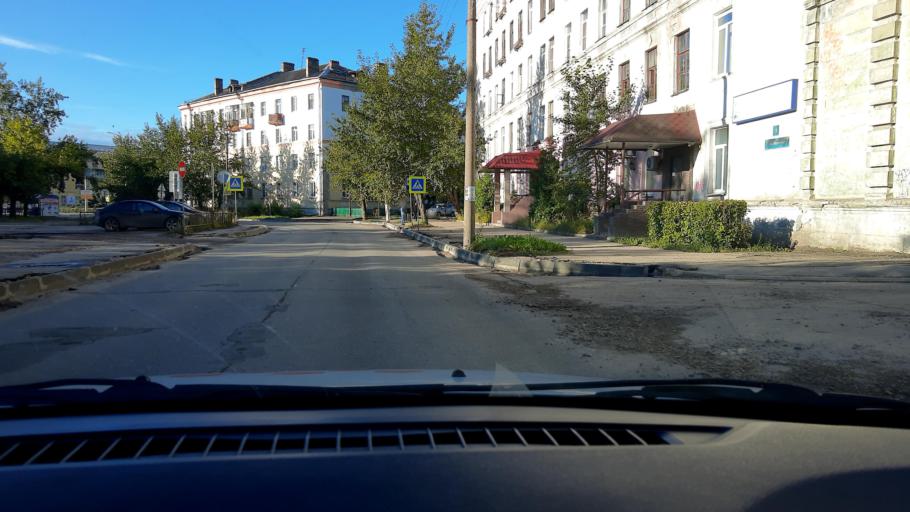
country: RU
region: Nizjnij Novgorod
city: Dzerzhinsk
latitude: 56.2444
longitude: 43.4717
